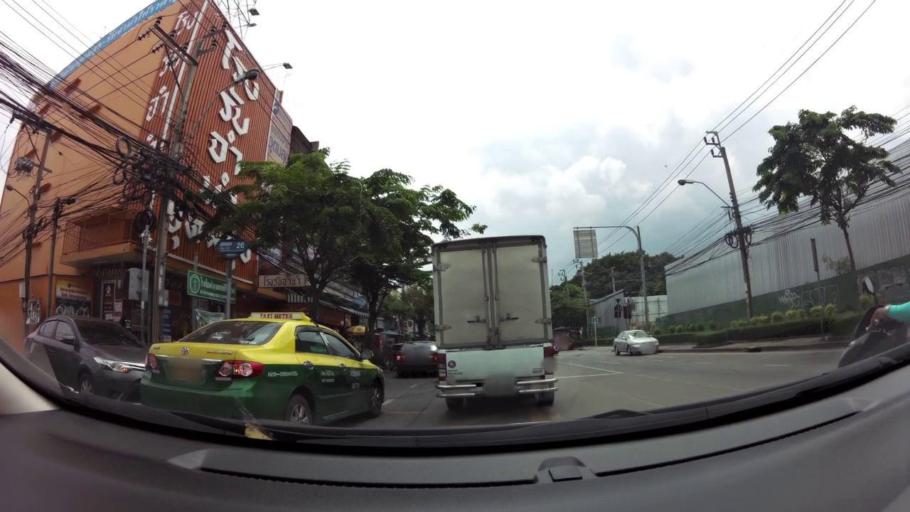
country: TH
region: Bangkok
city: Bang Na
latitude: 13.6785
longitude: 100.6177
